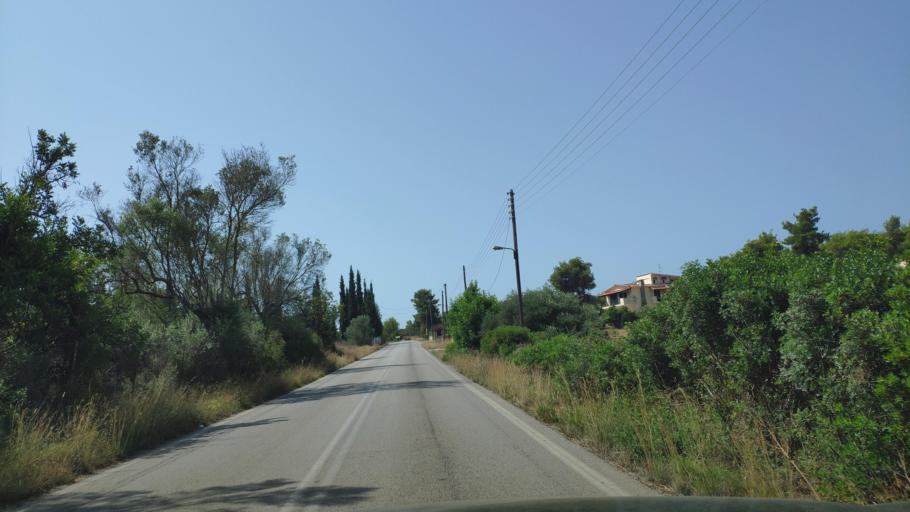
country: GR
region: Peloponnese
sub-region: Nomos Argolidos
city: Porto Cheli
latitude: 37.3046
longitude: 23.1647
